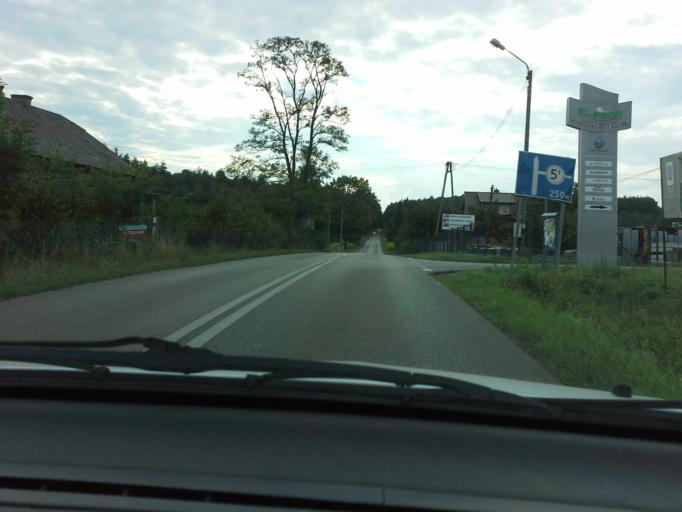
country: PL
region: Lesser Poland Voivodeship
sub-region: Powiat chrzanowski
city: Plaza
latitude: 50.1211
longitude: 19.4533
